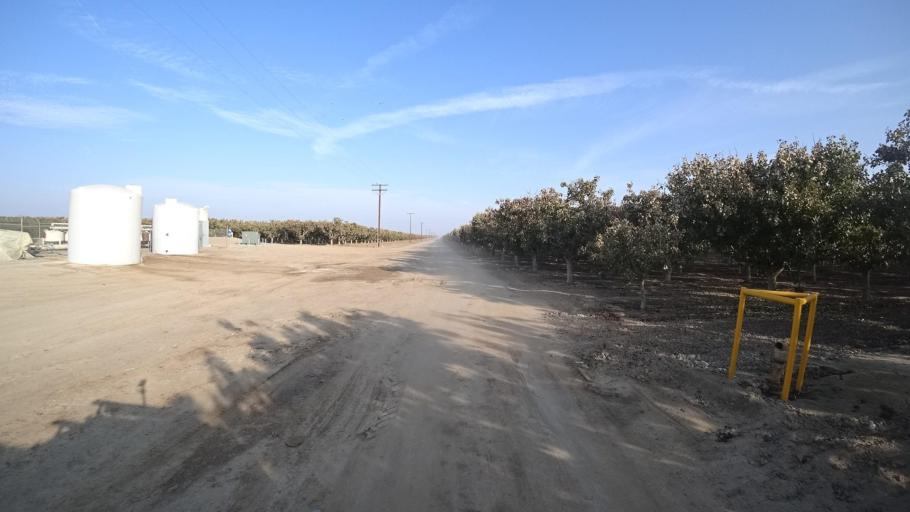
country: US
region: California
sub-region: Kern County
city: McFarland
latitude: 35.7266
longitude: -119.1873
